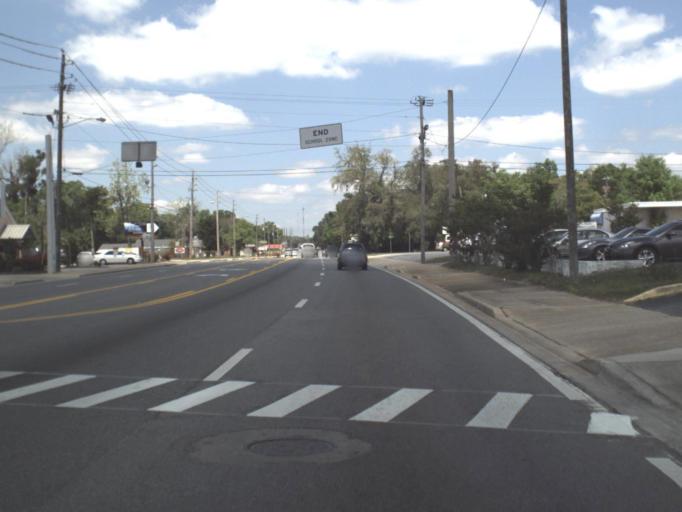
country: US
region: Florida
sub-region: Santa Rosa County
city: Milton
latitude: 30.6344
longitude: -87.0431
